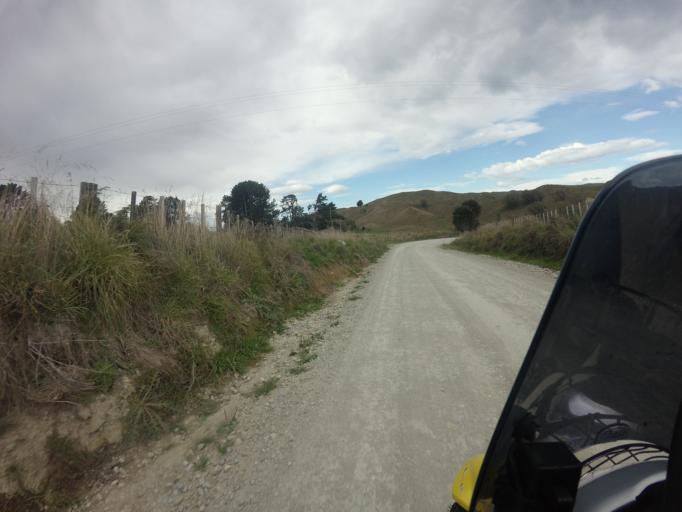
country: NZ
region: Hawke's Bay
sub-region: Wairoa District
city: Wairoa
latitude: -38.6019
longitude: 177.5063
